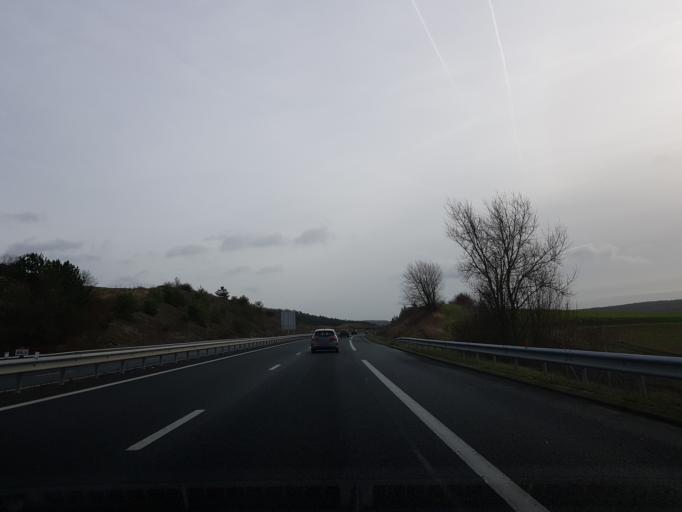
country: FR
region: Bourgogne
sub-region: Departement de l'Yonne
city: Soucy
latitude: 48.2583
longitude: 3.3280
